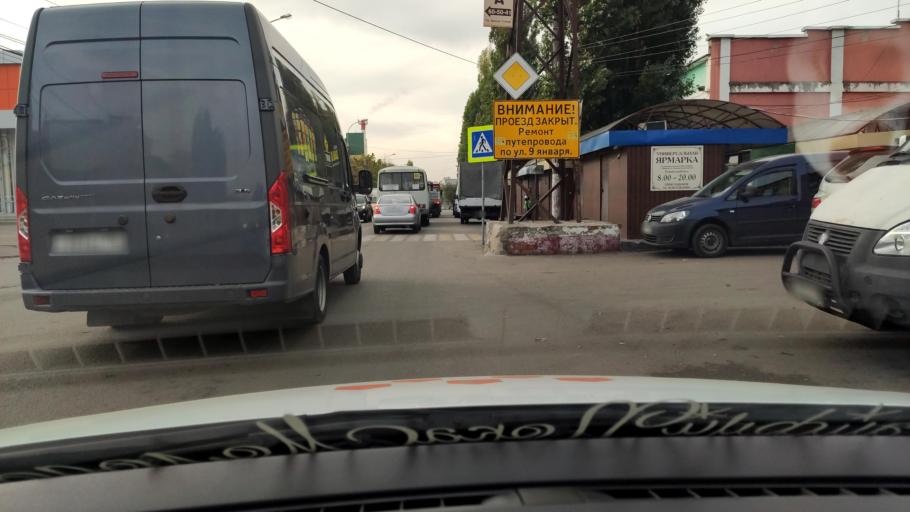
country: RU
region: Voronezj
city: Voronezh
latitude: 51.6739
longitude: 39.1556
